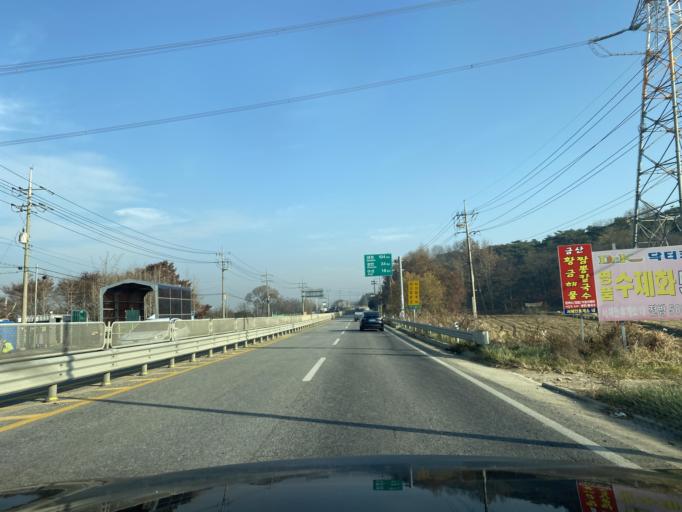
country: KR
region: Chungcheongnam-do
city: Yesan
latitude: 36.7415
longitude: 126.8599
